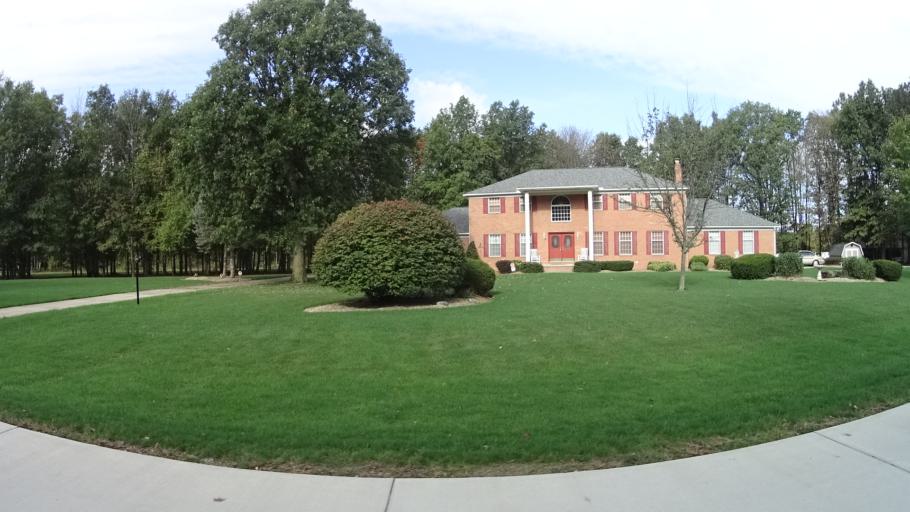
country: US
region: Ohio
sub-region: Lorain County
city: Grafton
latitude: 41.3255
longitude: -82.0579
